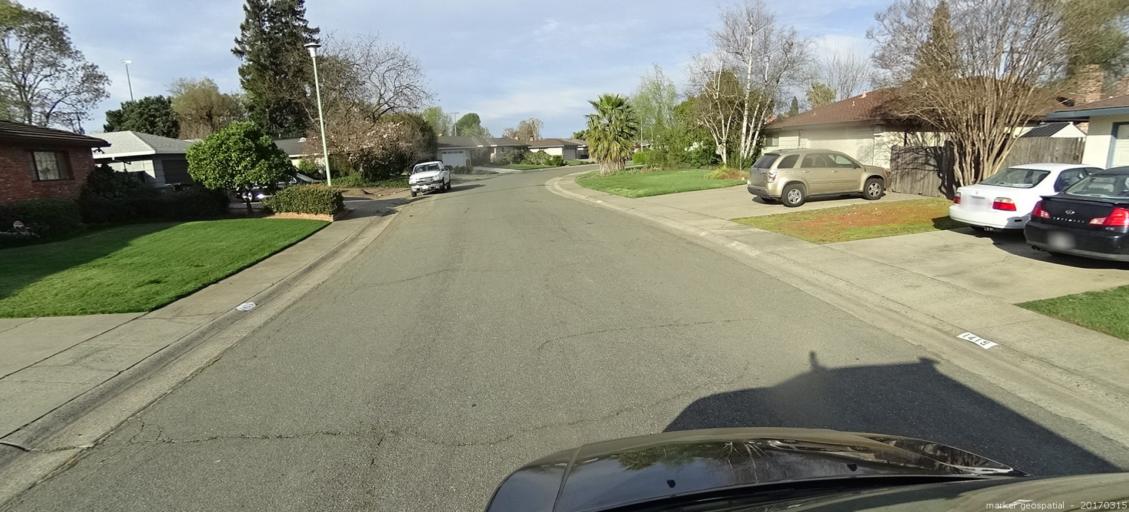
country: US
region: California
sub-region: Sacramento County
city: Parkway
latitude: 38.5027
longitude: -121.5086
